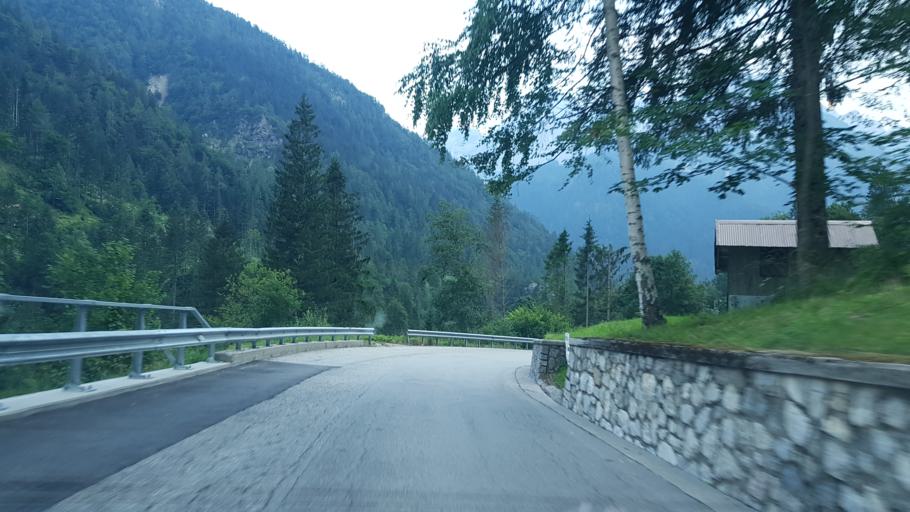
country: IT
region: Friuli Venezia Giulia
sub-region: Provincia di Udine
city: Forni Avoltri
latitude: 46.5992
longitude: 12.7769
